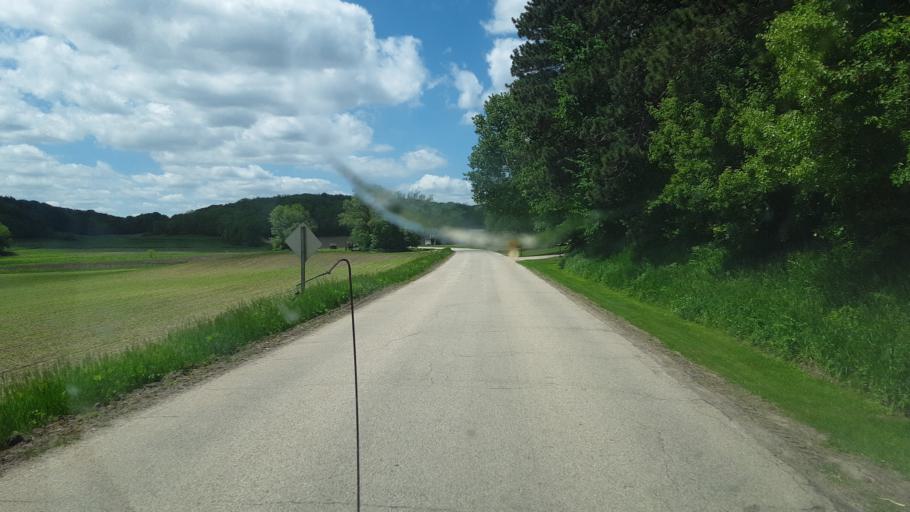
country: US
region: Wisconsin
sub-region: Sauk County
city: Reedsburg
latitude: 43.5758
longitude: -90.0020
